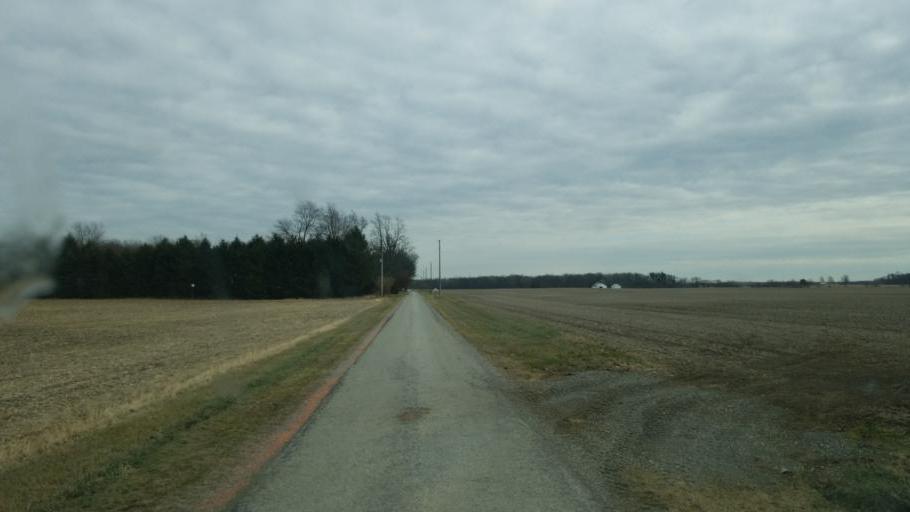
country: US
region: Ohio
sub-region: Crawford County
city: Bucyrus
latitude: 40.7468
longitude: -82.9636
